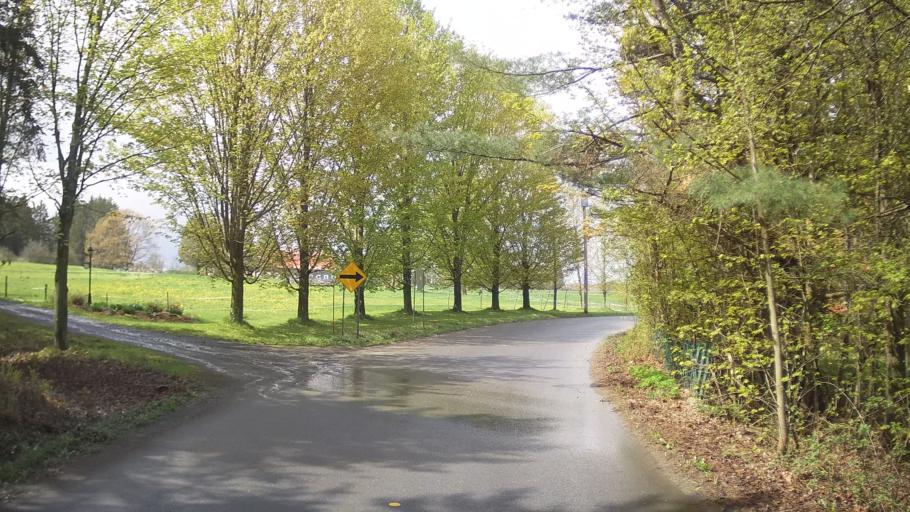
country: CA
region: Quebec
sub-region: Monteregie
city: Cowansville
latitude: 45.1735
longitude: -72.6664
